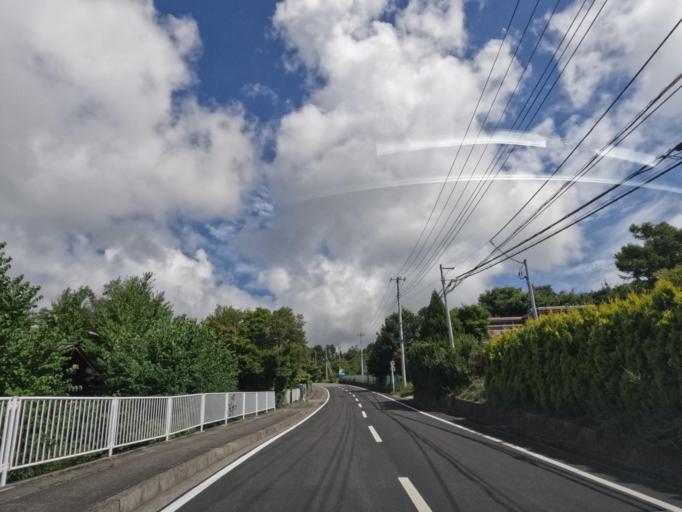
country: JP
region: Yamanashi
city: Nirasaki
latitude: 35.8912
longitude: 138.4105
